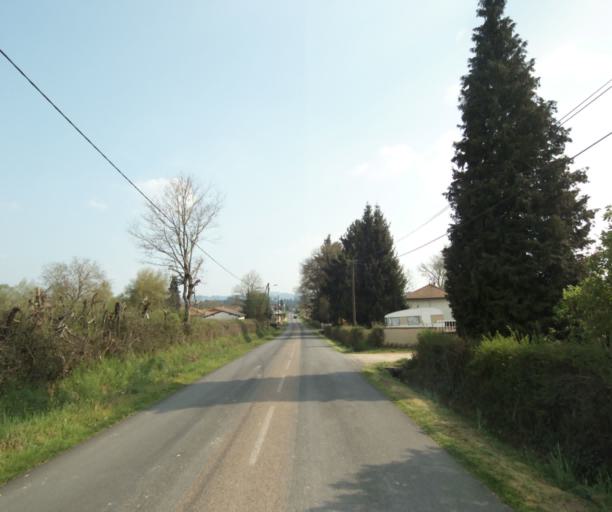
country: FR
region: Bourgogne
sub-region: Departement de Saone-et-Loire
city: Charolles
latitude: 46.4871
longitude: 4.4356
